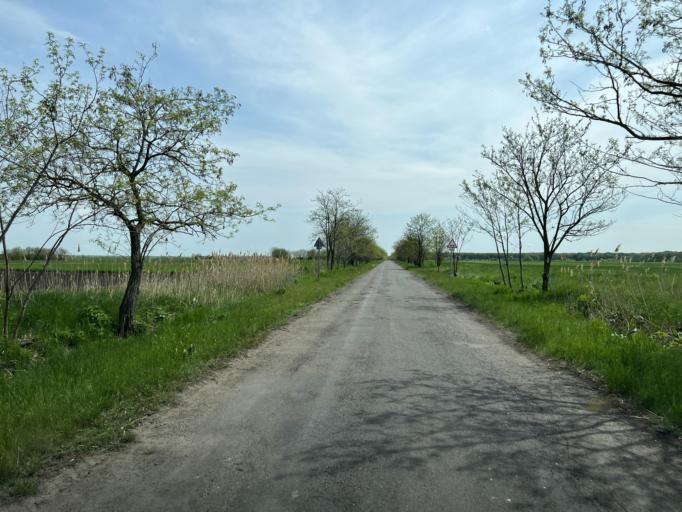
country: HU
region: Pest
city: Tapiogyorgye
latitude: 47.2946
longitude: 19.9947
